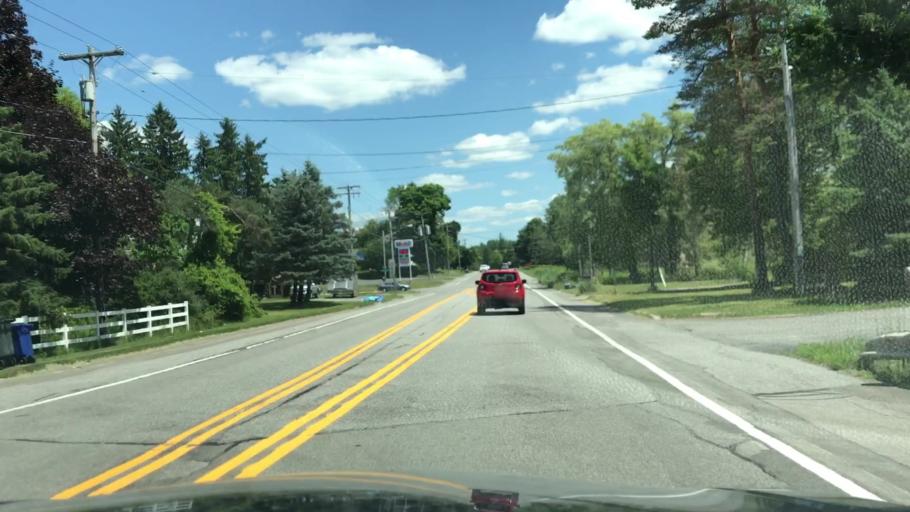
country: US
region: New York
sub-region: Erie County
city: East Aurora
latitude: 42.7678
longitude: -78.5543
